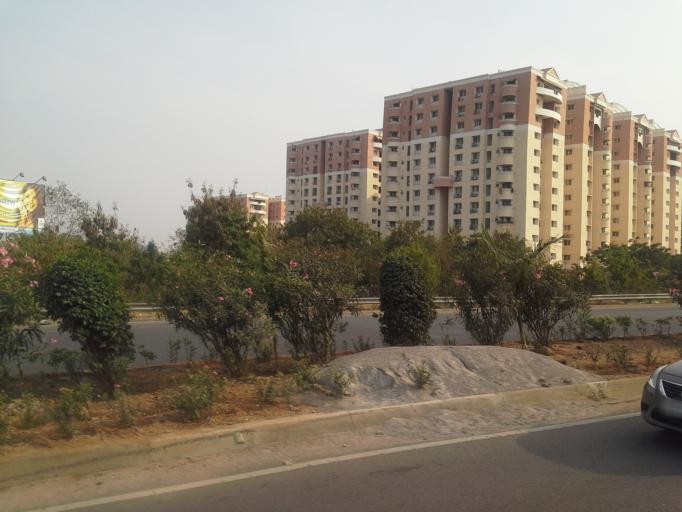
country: IN
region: Telangana
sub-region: Rangareddi
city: Kukatpalli
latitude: 17.4353
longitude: 78.3613
